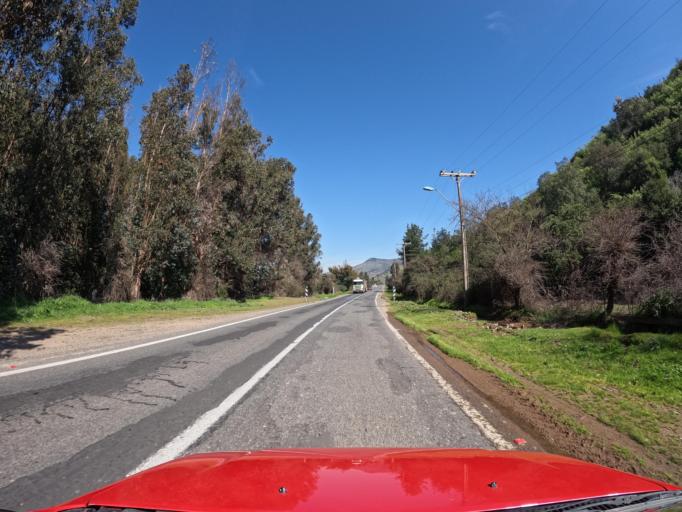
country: CL
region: Maule
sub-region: Provincia de Curico
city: Rauco
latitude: -35.0528
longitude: -71.6044
